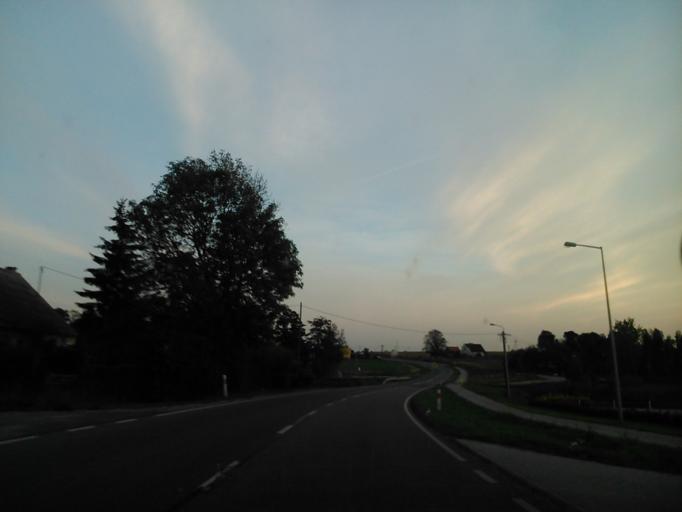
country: PL
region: Kujawsko-Pomorskie
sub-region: Powiat wabrzeski
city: Debowa Laka
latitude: 53.2015
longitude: 19.0371
